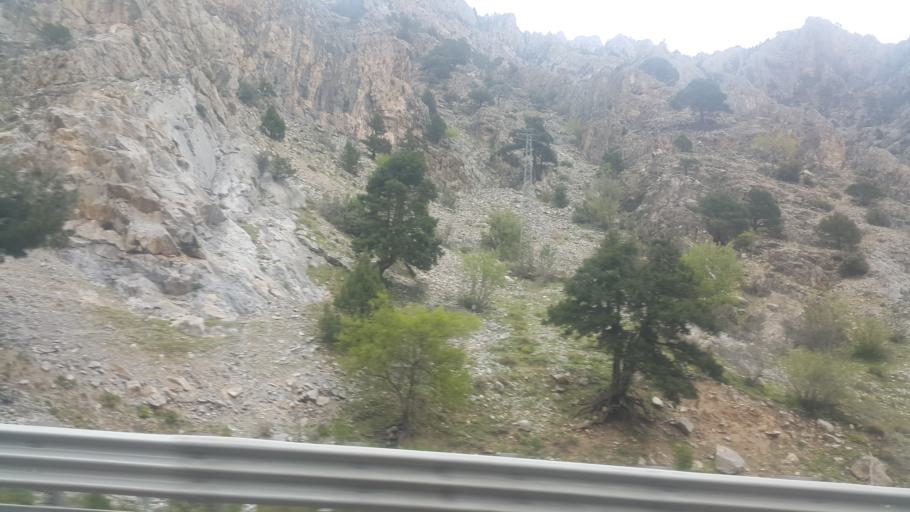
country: TR
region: Adana
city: Pozanti
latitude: 37.4823
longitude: 34.8521
